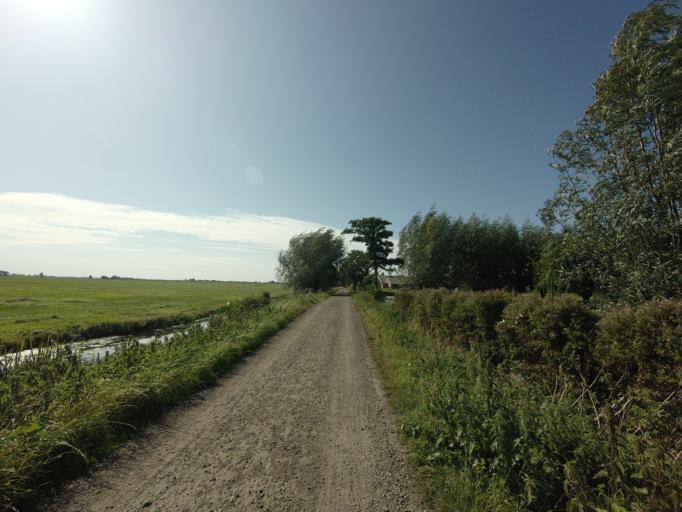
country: NL
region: South Holland
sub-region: Molenwaard
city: Liesveld
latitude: 51.9193
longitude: 4.8048
